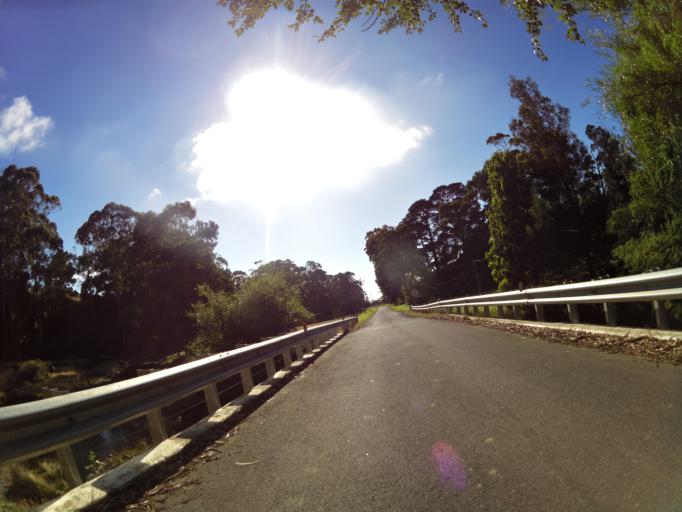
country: AU
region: Victoria
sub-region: Colac-Otway
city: Apollo Bay
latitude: -38.7651
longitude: 143.6337
